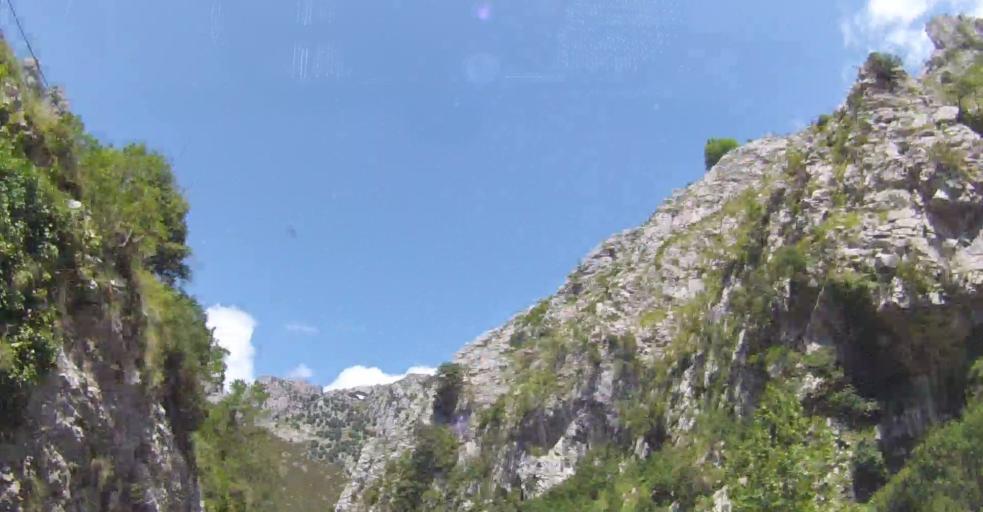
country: ES
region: Cantabria
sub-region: Provincia de Cantabria
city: Tresviso
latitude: 43.2722
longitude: -4.6364
